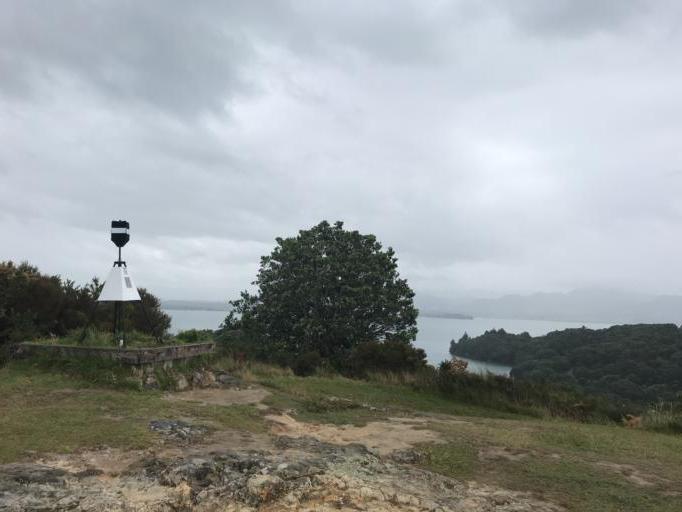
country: NZ
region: Bay of Plenty
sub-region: Western Bay of Plenty District
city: Waihi Beach
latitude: -37.4650
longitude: 175.9903
